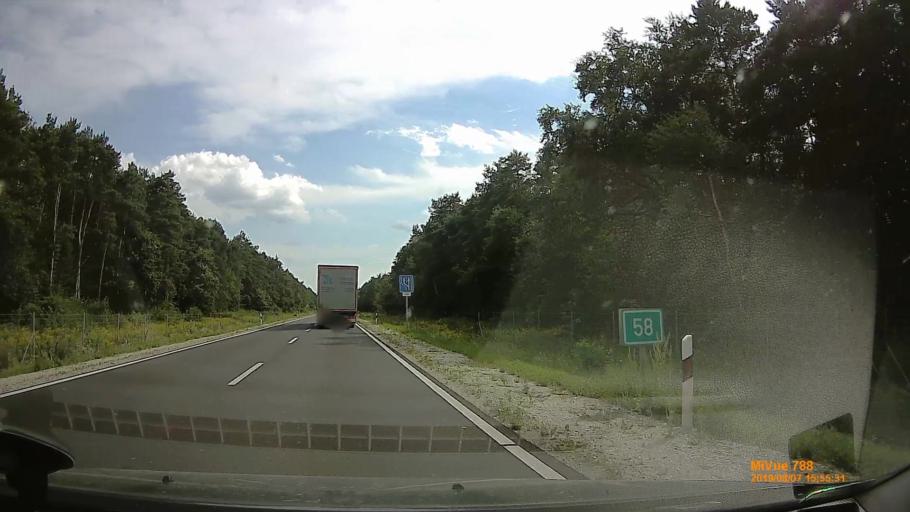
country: HU
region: Vas
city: Kormend
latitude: 47.0734
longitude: 16.6178
